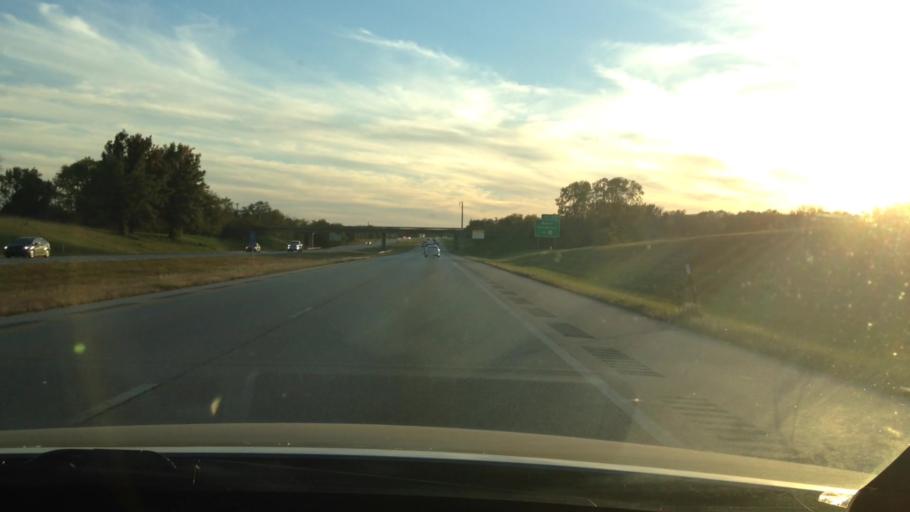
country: US
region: Kansas
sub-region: Johnson County
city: Olathe
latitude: 38.8278
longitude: -94.8563
